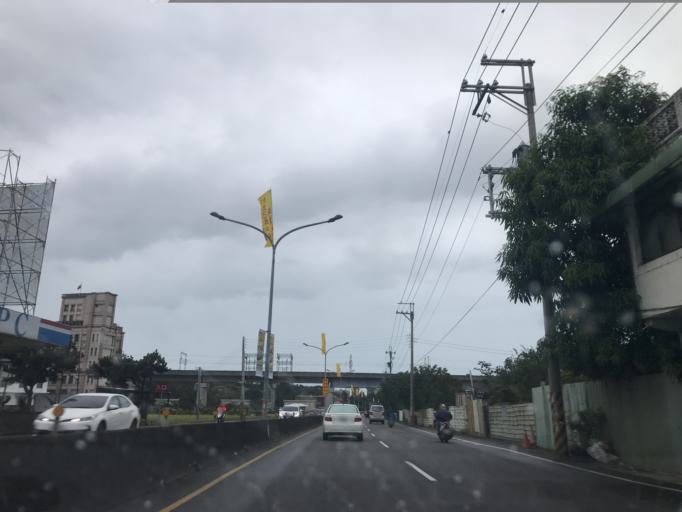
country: TW
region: Taiwan
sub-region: Hsinchu
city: Zhubei
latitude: 24.8274
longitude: 121.0483
